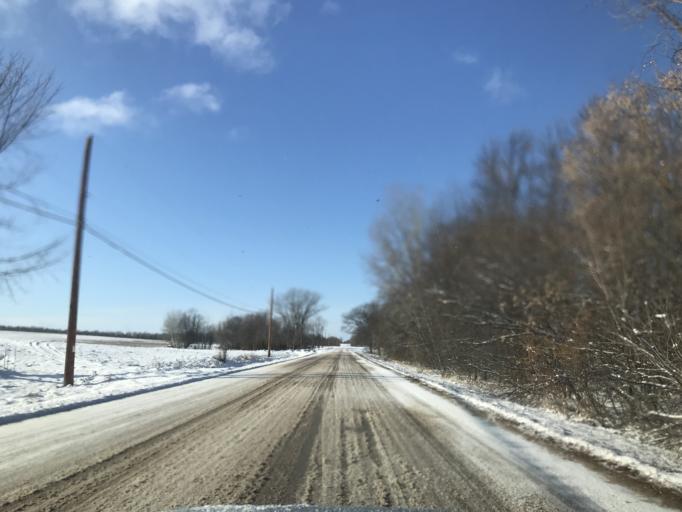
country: US
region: Wisconsin
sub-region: Door County
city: Sturgeon Bay
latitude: 44.8499
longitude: -87.4629
